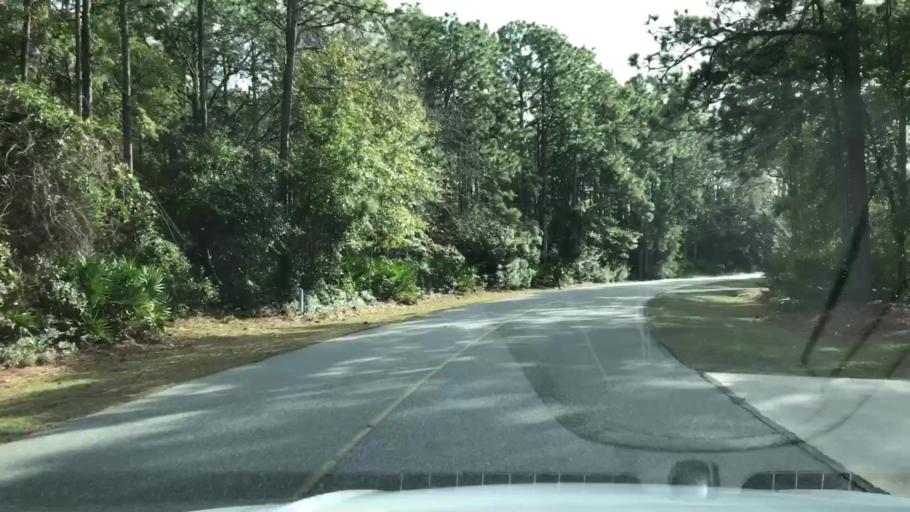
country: US
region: South Carolina
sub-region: Beaufort County
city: Hilton Head Island
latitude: 32.2439
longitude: -80.7070
